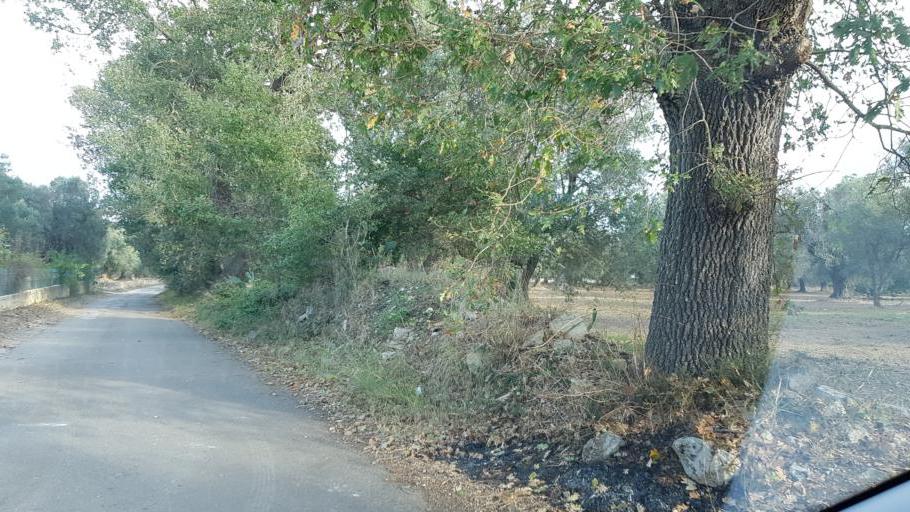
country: IT
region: Apulia
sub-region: Provincia di Brindisi
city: Oria
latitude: 40.5012
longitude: 17.6729
